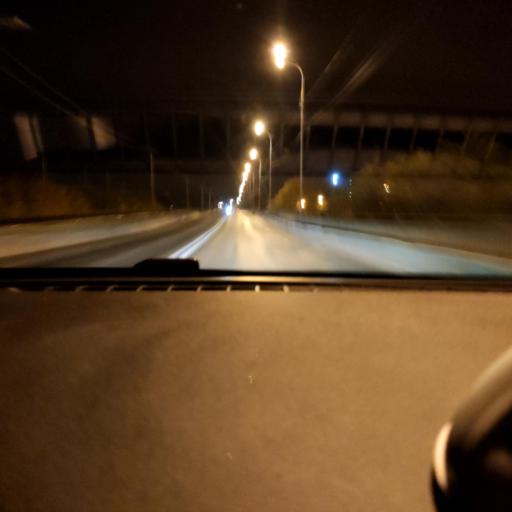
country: RU
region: Samara
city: Smyshlyayevka
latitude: 53.2182
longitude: 50.2905
